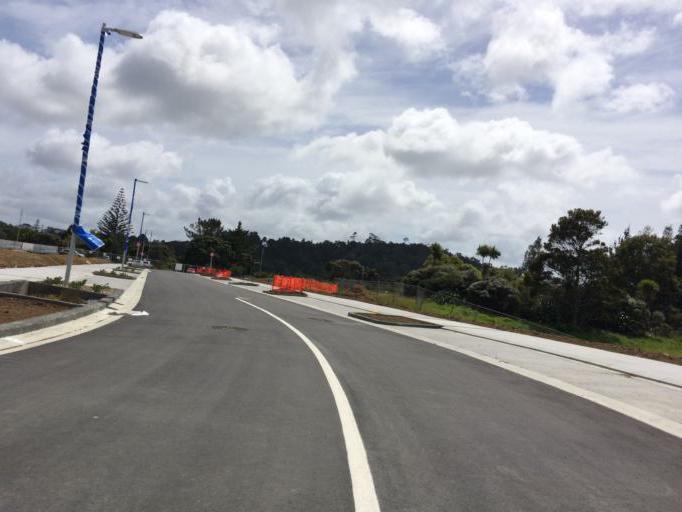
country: NZ
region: Auckland
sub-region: Auckland
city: North Shore
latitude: -36.7907
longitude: 174.6702
